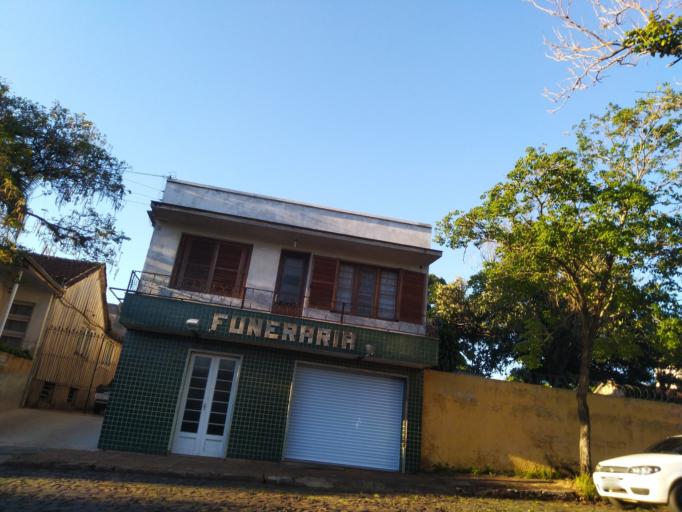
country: BR
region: Rio Grande do Sul
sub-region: Sao Borja
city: Sao Borja
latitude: -28.6615
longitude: -56.0093
